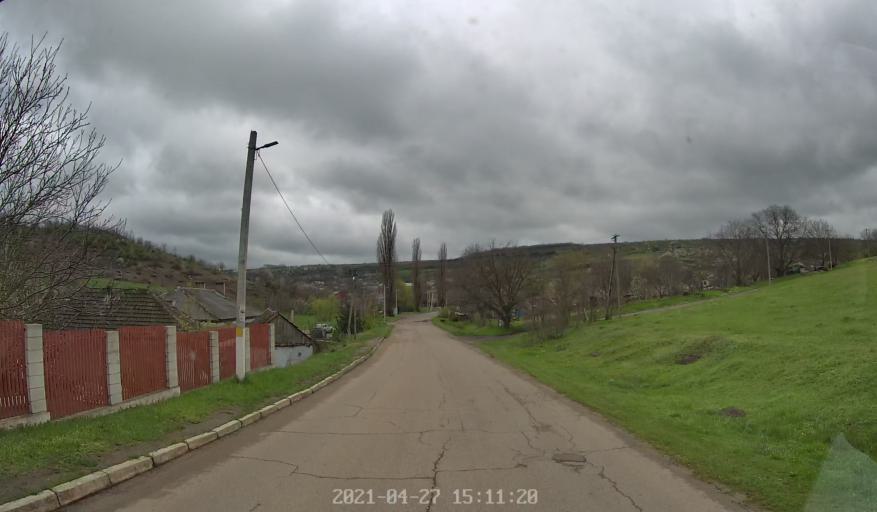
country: MD
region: Chisinau
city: Vadul lui Voda
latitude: 47.0325
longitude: 29.0279
